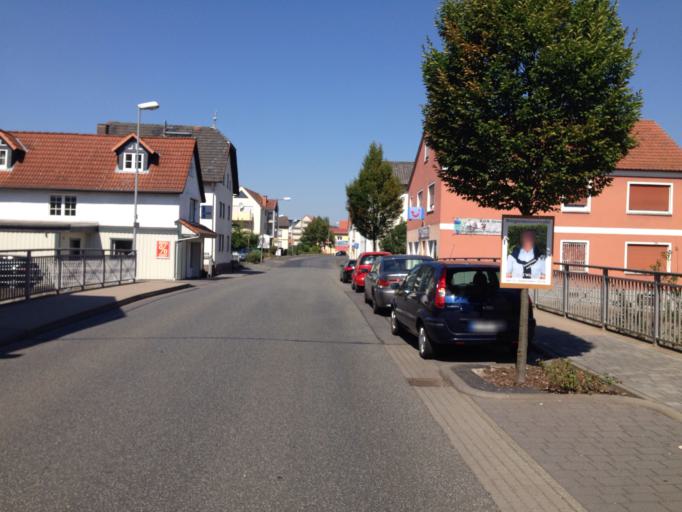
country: DE
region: Hesse
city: Lollar
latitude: 50.6452
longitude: 8.7035
